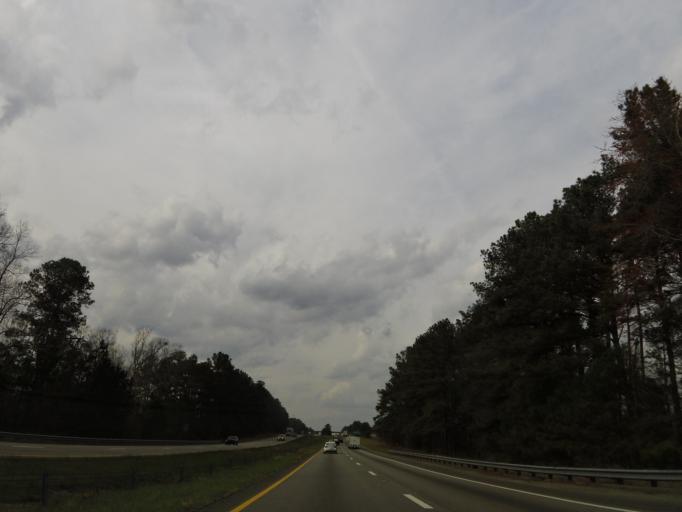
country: US
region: South Carolina
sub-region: Calhoun County
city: Saint Matthews
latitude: 33.6270
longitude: -80.8723
